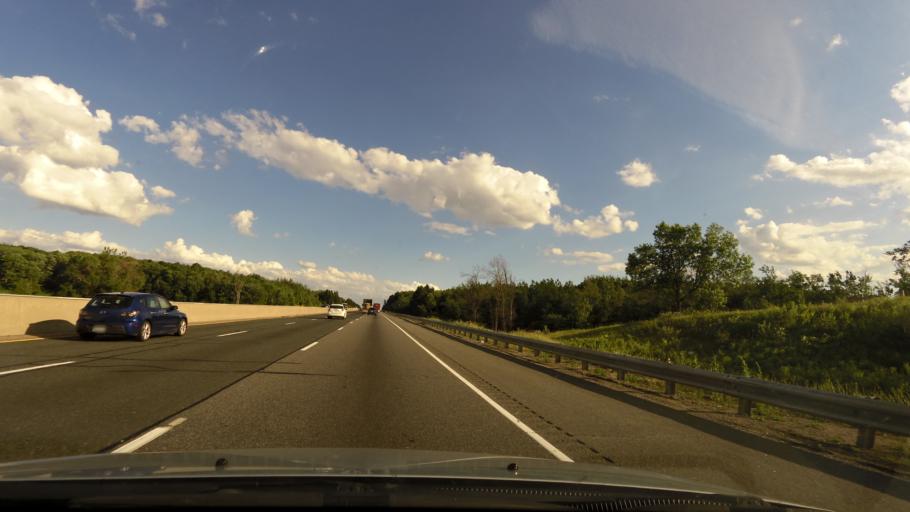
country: CA
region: Ontario
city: Newmarket
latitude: 43.9703
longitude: -79.5781
